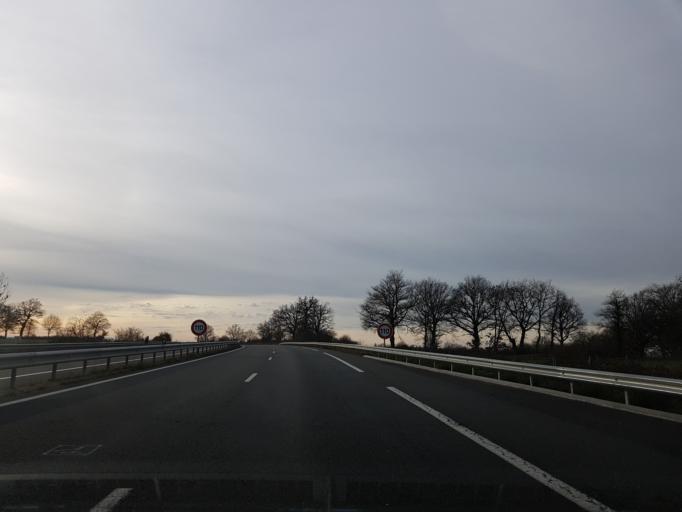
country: FR
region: Auvergne
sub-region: Departement de l'Allier
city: Montmarault
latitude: 46.3602
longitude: 3.0105
